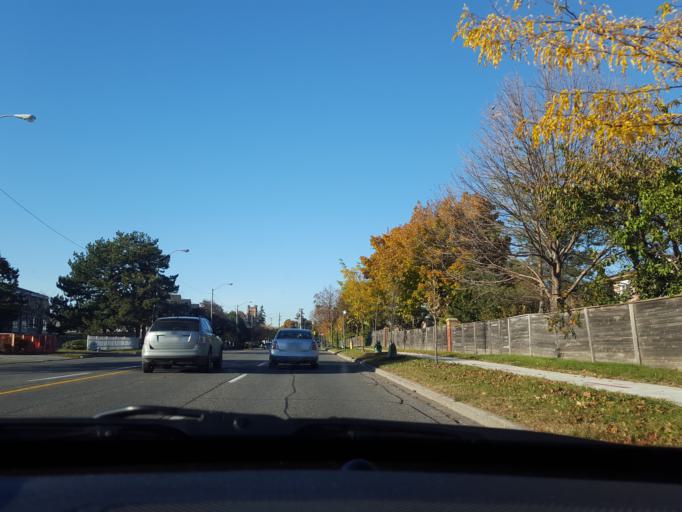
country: CA
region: Ontario
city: Markham
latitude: 43.8256
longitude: -79.2862
